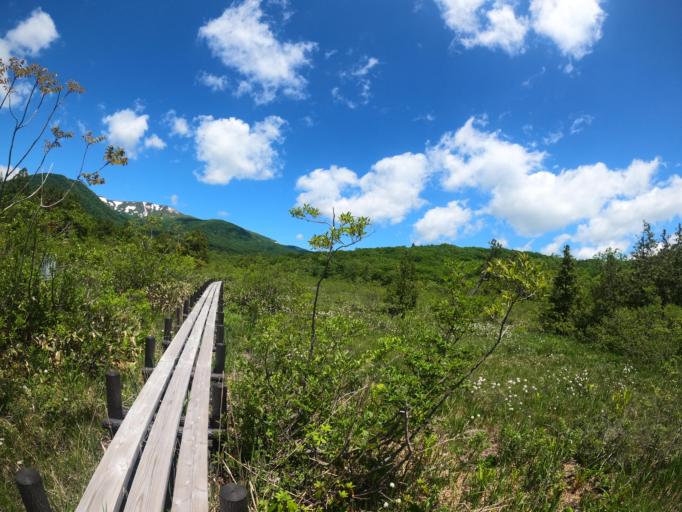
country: JP
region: Iwate
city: Ichinoseki
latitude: 38.9146
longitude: 140.8035
